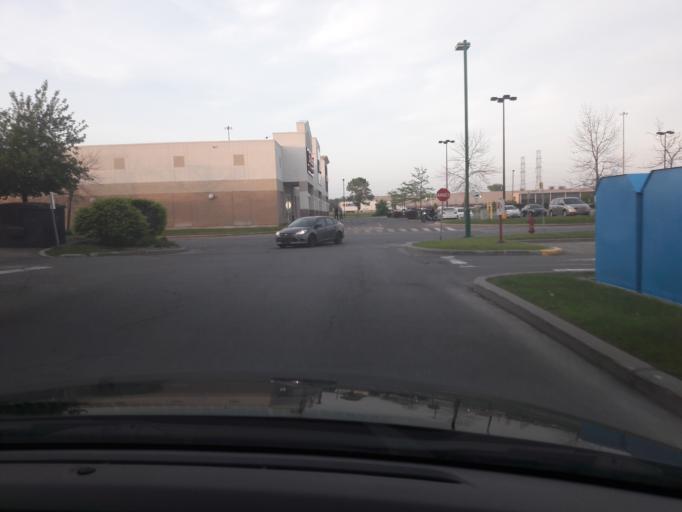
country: CA
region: Quebec
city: Dollard-Des Ormeaux
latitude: 45.5264
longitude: -73.7825
